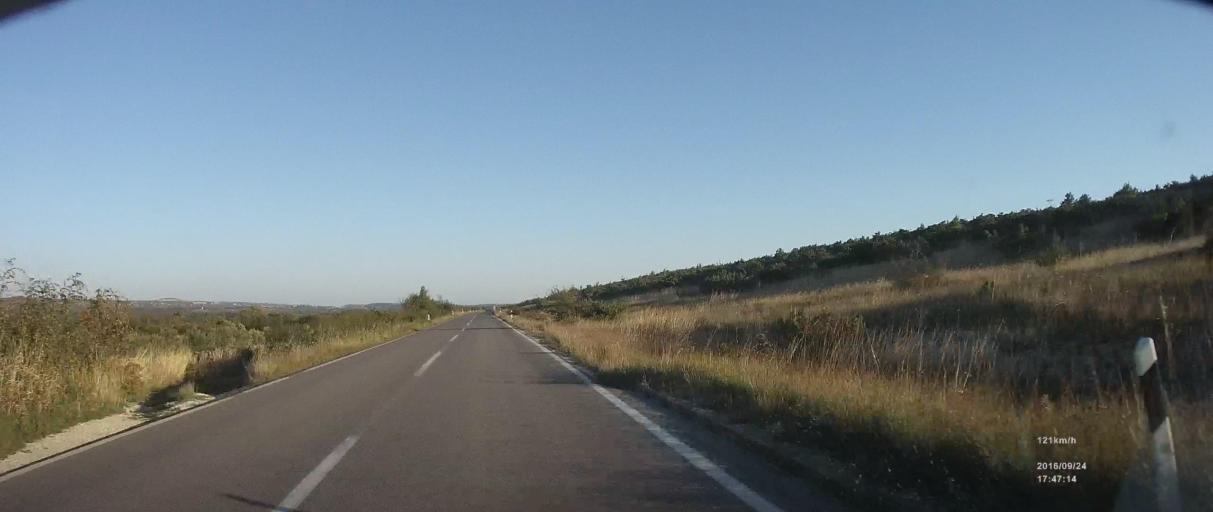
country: HR
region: Zadarska
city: Polaca
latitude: 44.0776
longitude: 15.5200
